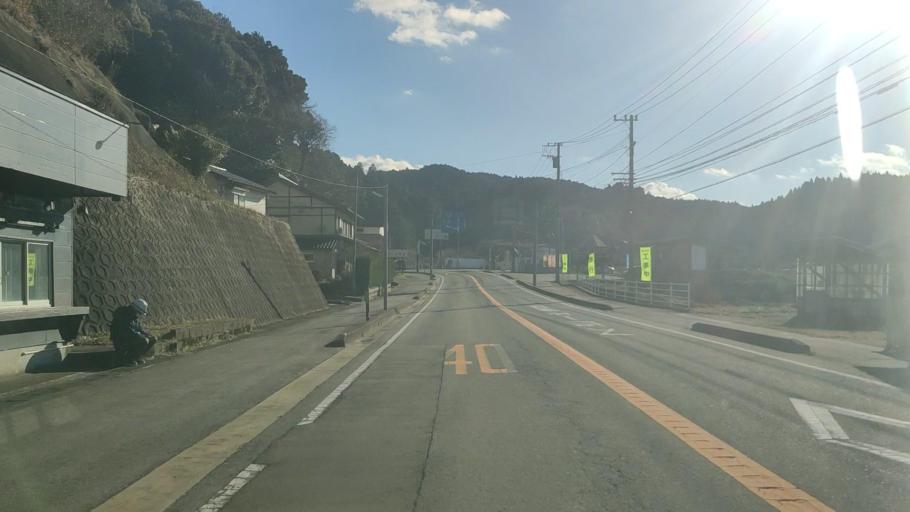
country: JP
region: Saga Prefecture
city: Kanzakimachi-kanzaki
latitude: 33.4239
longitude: 130.2776
